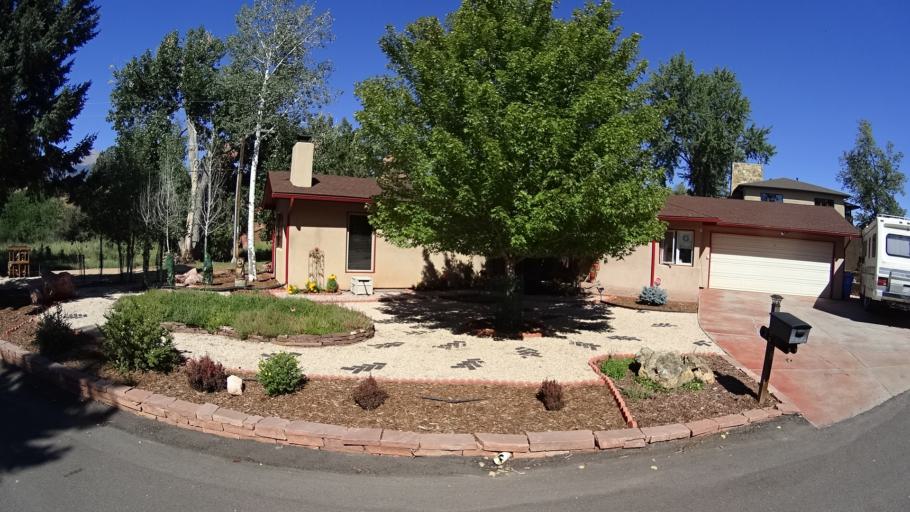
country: US
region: Colorado
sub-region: El Paso County
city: Manitou Springs
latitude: 38.8670
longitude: -104.8835
